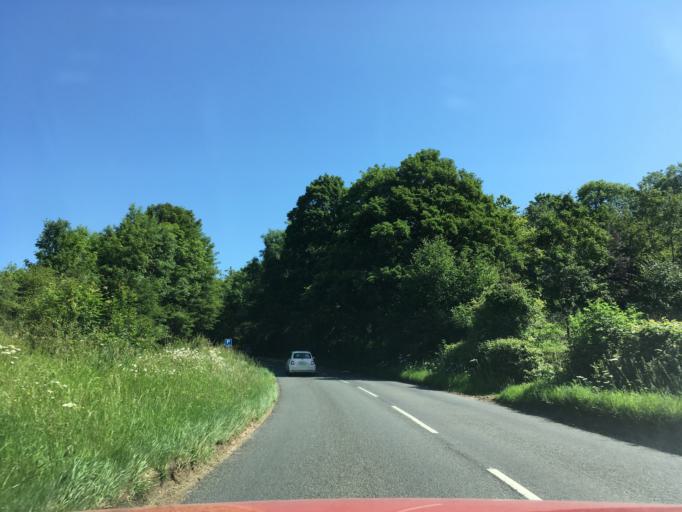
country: GB
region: England
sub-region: Gloucestershire
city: Westfield
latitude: 51.9070
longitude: -1.8090
